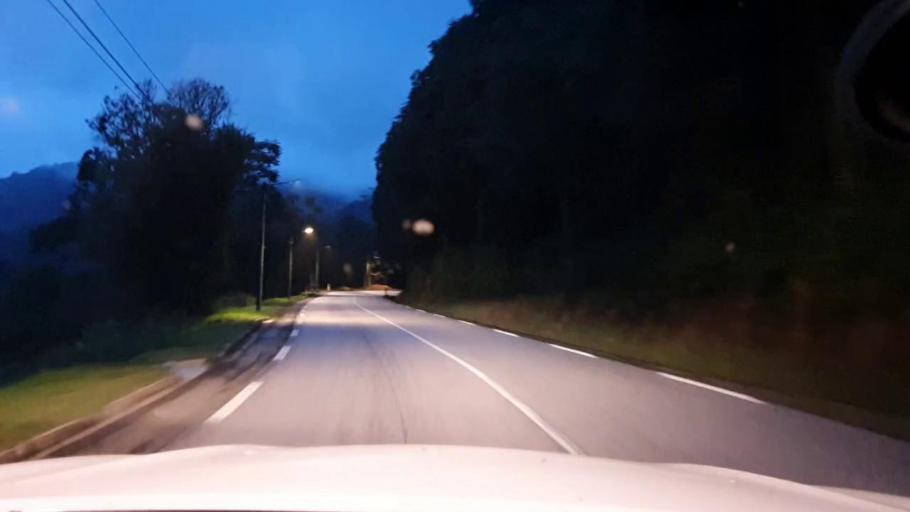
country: RW
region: Southern Province
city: Nzega
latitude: -2.5324
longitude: 29.3899
